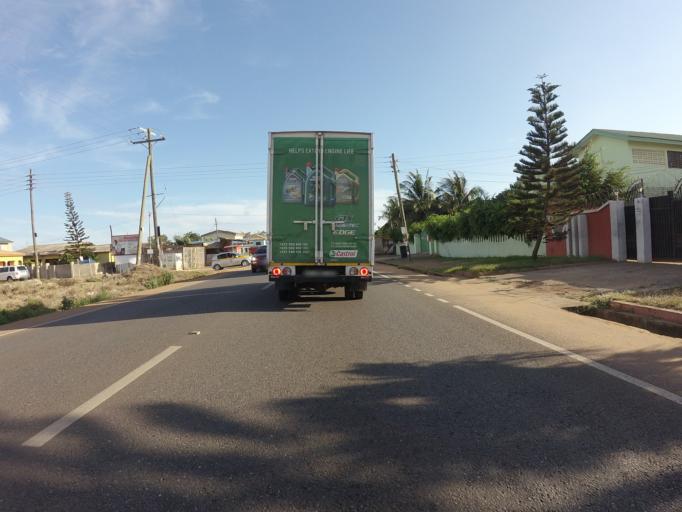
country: GH
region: Greater Accra
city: Nungua
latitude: 5.6414
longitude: -0.0925
